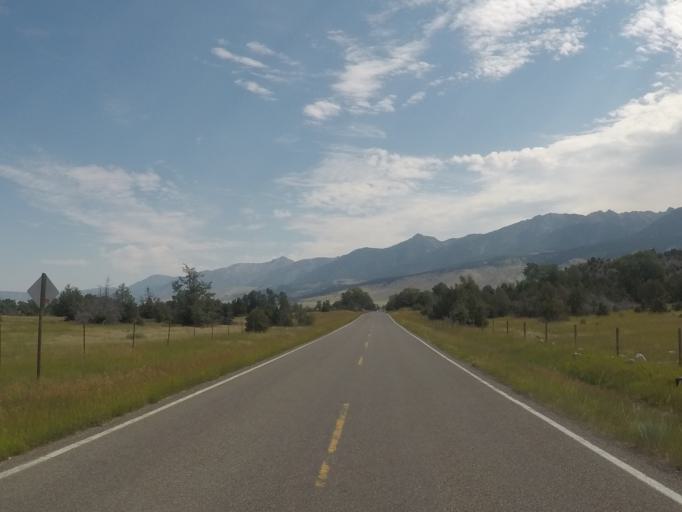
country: US
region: Montana
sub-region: Park County
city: Livingston
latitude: 45.4173
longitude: -110.6397
